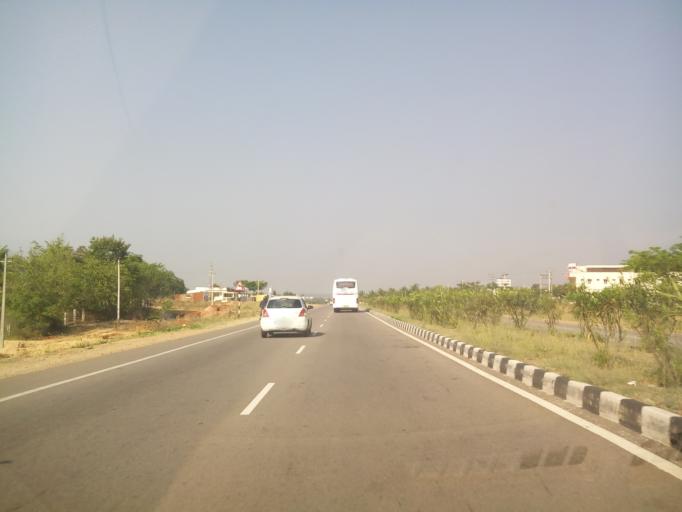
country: IN
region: Karnataka
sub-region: Mandya
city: Belluru
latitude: 12.9881
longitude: 76.8763
